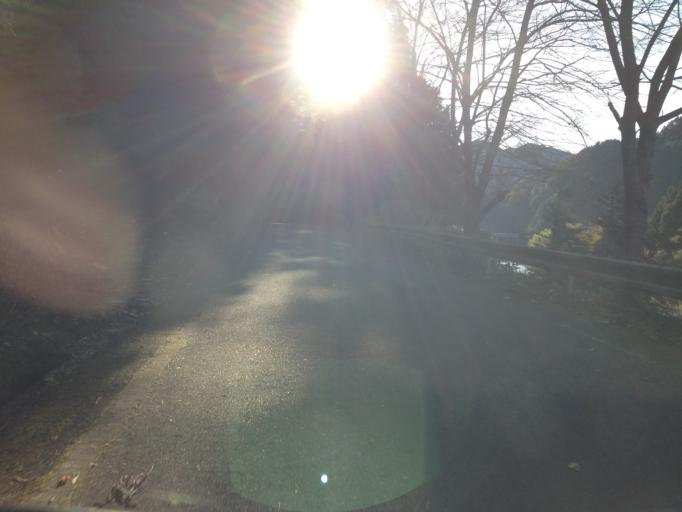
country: JP
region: Gifu
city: Mitake
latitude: 35.6075
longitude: 137.1810
